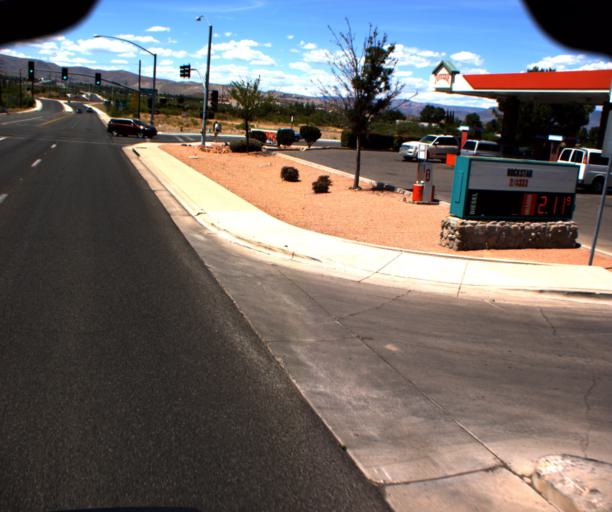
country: US
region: Arizona
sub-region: Yavapai County
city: Cottonwood
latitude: 34.7376
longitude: -112.0348
